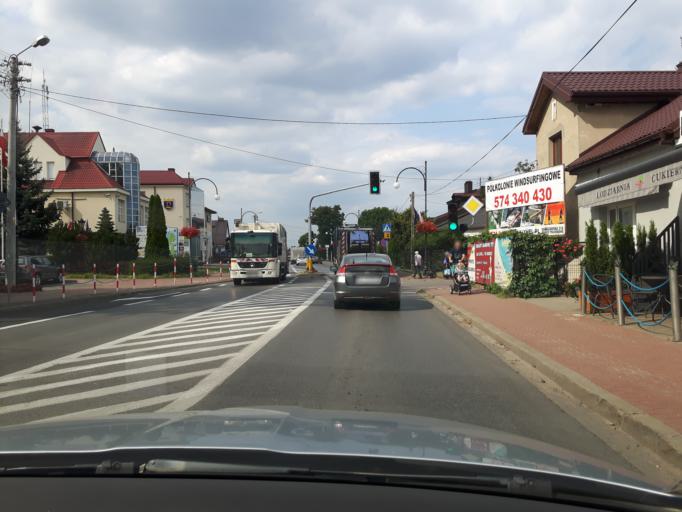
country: PL
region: Masovian Voivodeship
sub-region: Powiat legionowski
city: Nieporet
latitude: 52.4207
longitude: 21.0361
